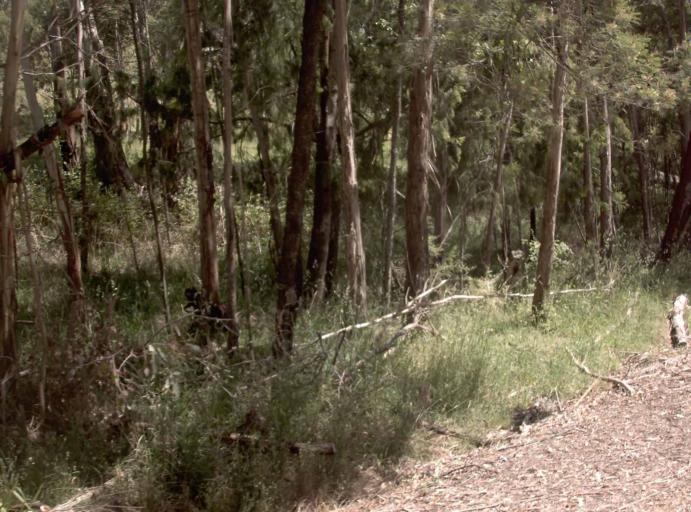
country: AU
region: Victoria
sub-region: East Gippsland
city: Lakes Entrance
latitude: -37.3485
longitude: 148.2285
